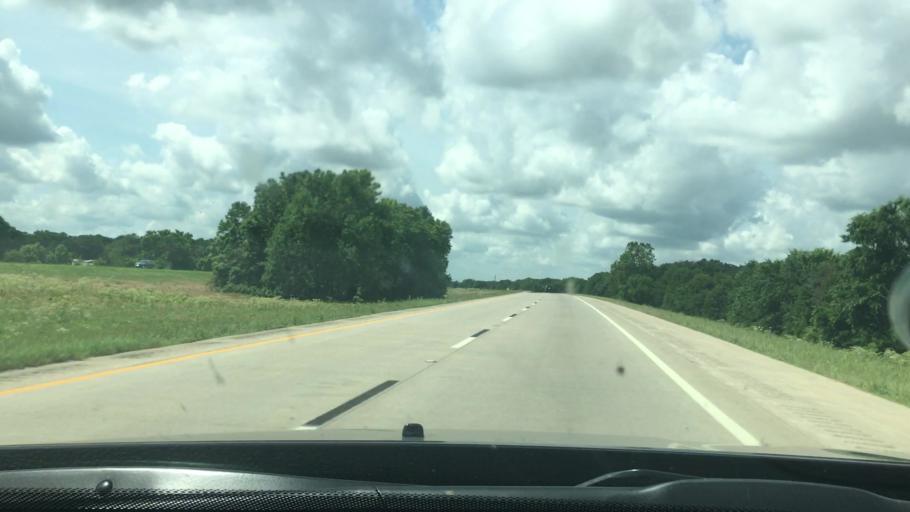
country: US
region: Oklahoma
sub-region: Love County
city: Marietta
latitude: 33.8125
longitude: -97.1339
